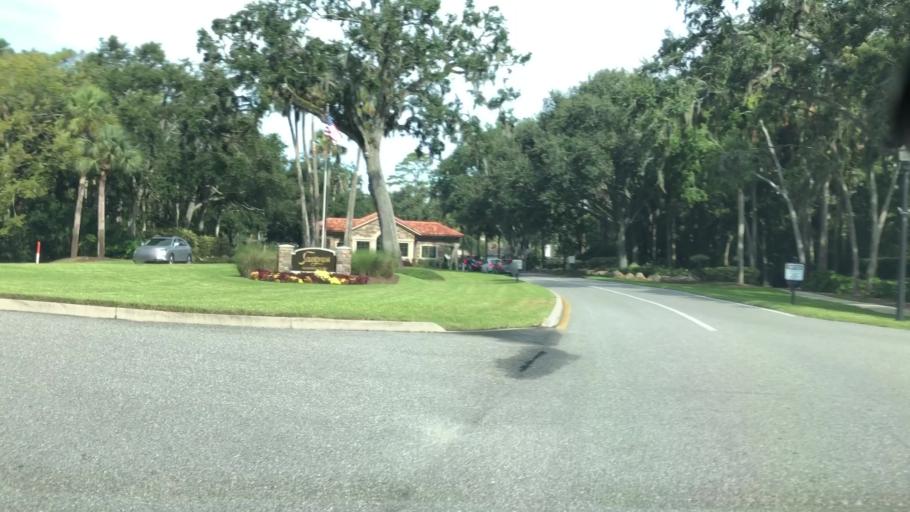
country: US
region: Florida
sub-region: Saint Johns County
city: Sawgrass
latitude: 30.2054
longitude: -81.3844
